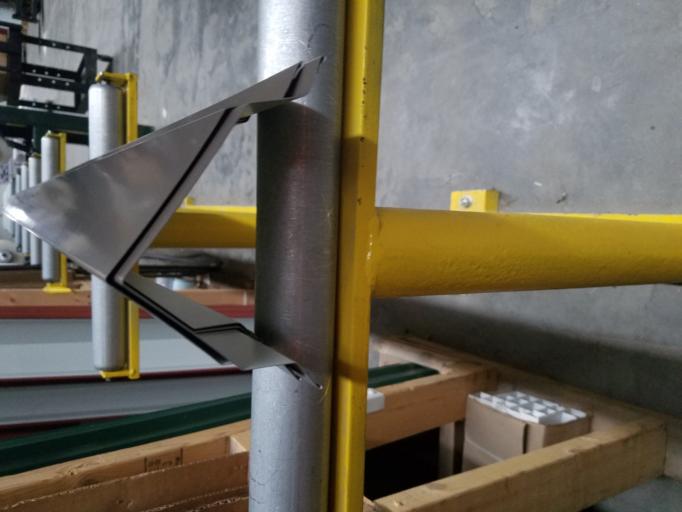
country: US
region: Michigan
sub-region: Missaukee County
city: Lake City
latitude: 44.2081
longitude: -85.1417
